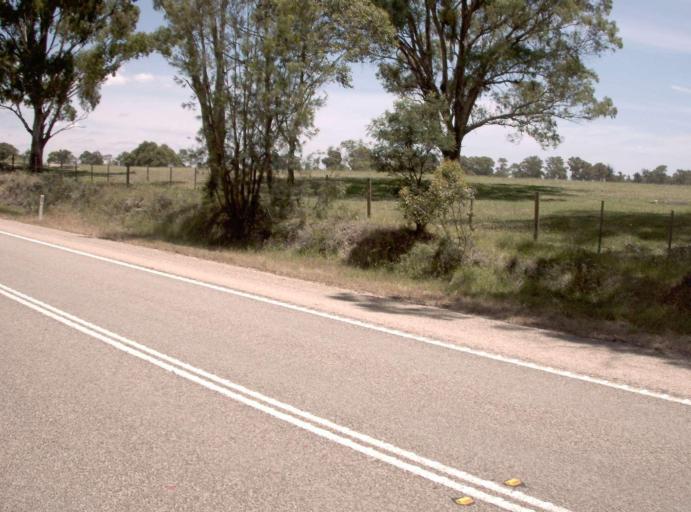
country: AU
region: Victoria
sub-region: East Gippsland
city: Bairnsdale
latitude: -37.7750
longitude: 147.6881
